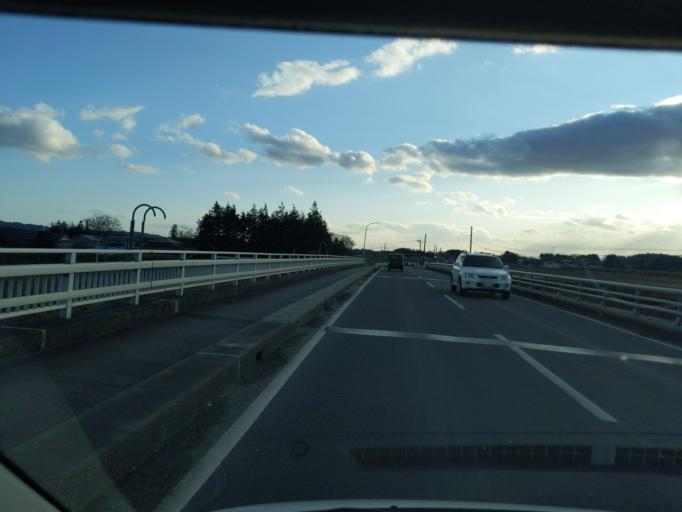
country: JP
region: Miyagi
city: Kogota
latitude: 38.6452
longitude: 141.0744
